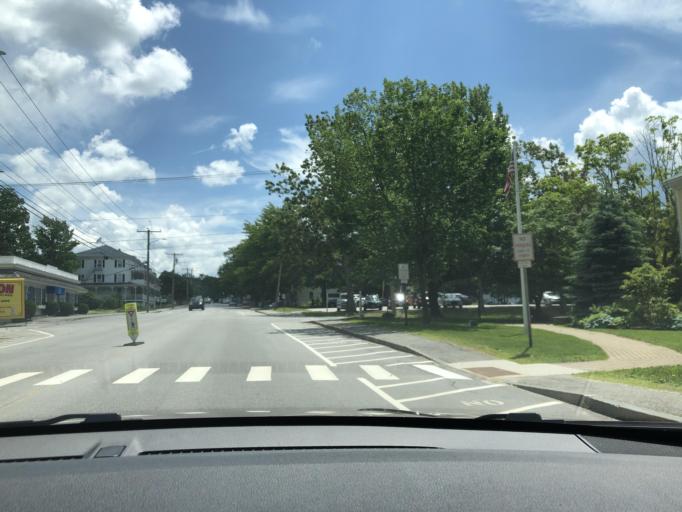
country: US
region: New Hampshire
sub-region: Merrimack County
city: New London
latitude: 43.4145
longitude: -71.9853
